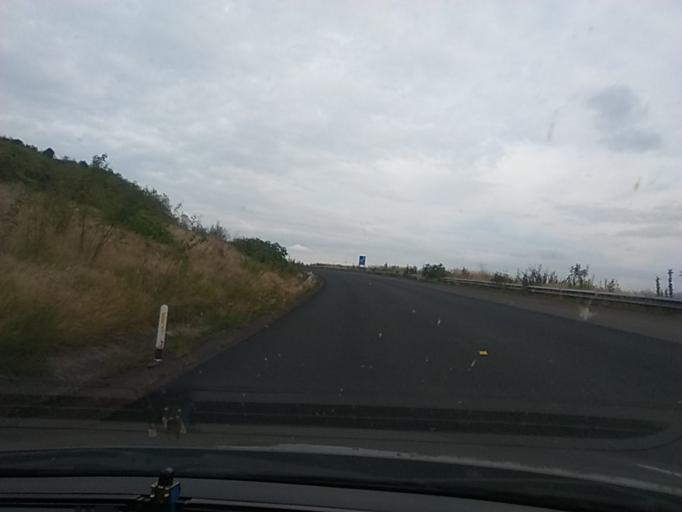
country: MX
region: Mexico
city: Huaniqueo de Morales
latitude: 19.8906
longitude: -101.5634
